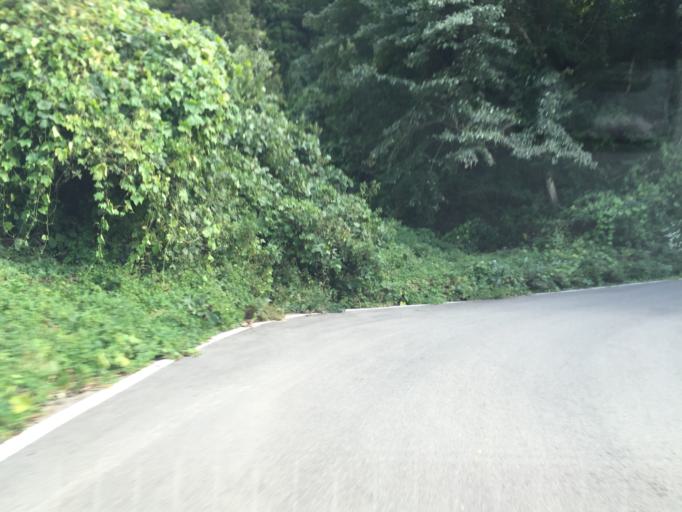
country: JP
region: Fukushima
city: Hobaramachi
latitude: 37.7726
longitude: 140.5212
